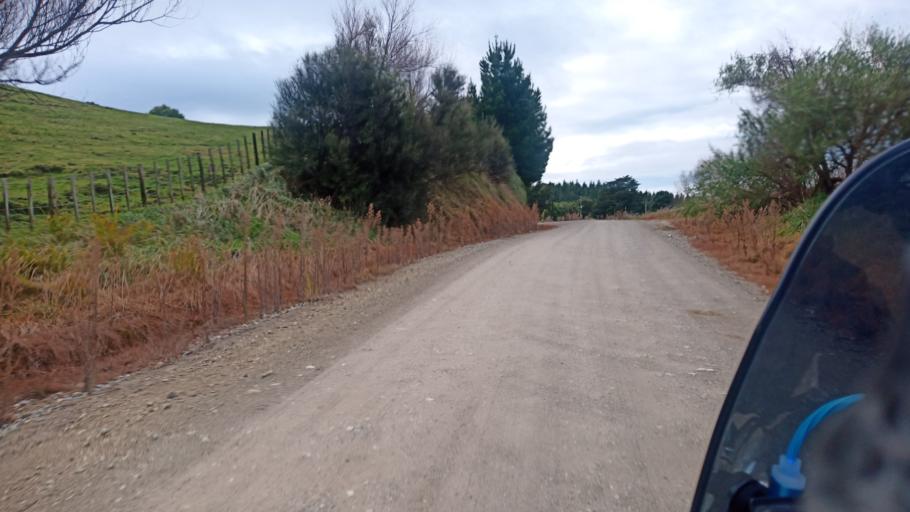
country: NZ
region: Gisborne
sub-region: Gisborne District
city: Gisborne
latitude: -38.3773
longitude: 177.9659
